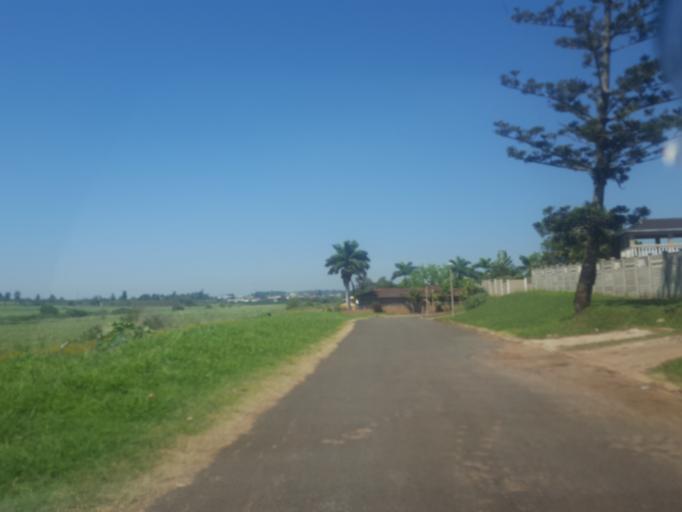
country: ZA
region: KwaZulu-Natal
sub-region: uThungulu District Municipality
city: Empangeni
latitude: -28.7524
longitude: 31.9085
